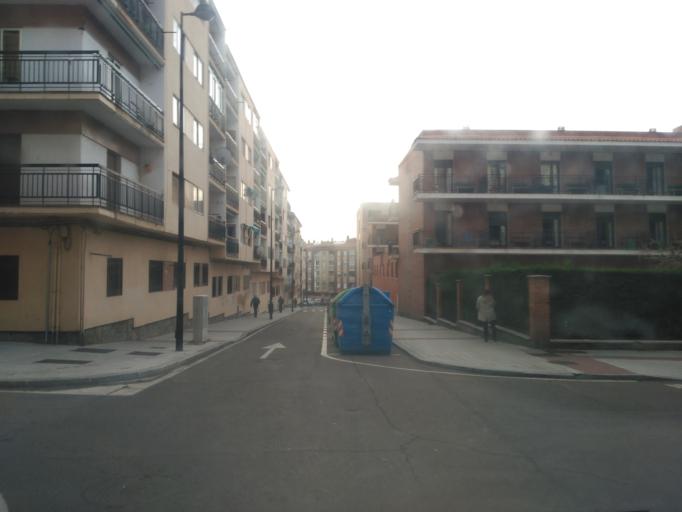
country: ES
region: Castille and Leon
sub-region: Provincia de Salamanca
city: Salamanca
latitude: 40.9652
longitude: -5.6518
